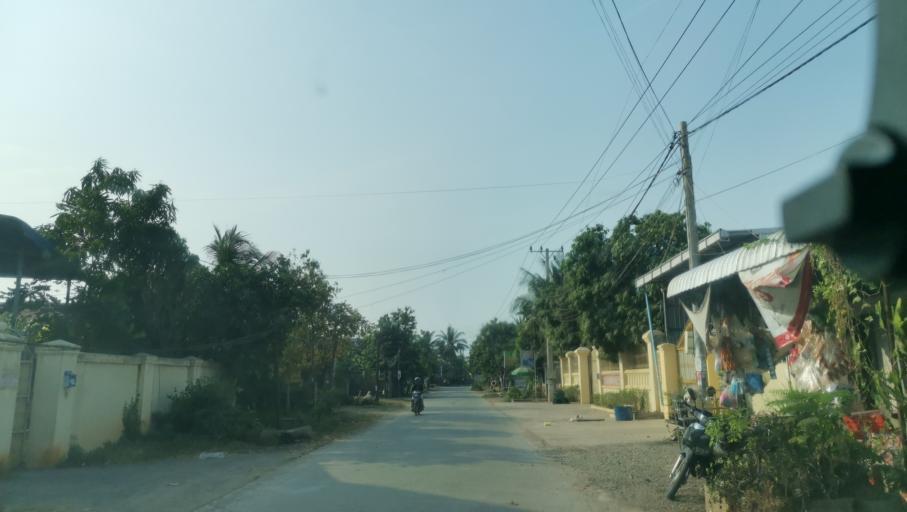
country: KH
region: Battambang
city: Battambang
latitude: 13.0872
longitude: 103.1933
